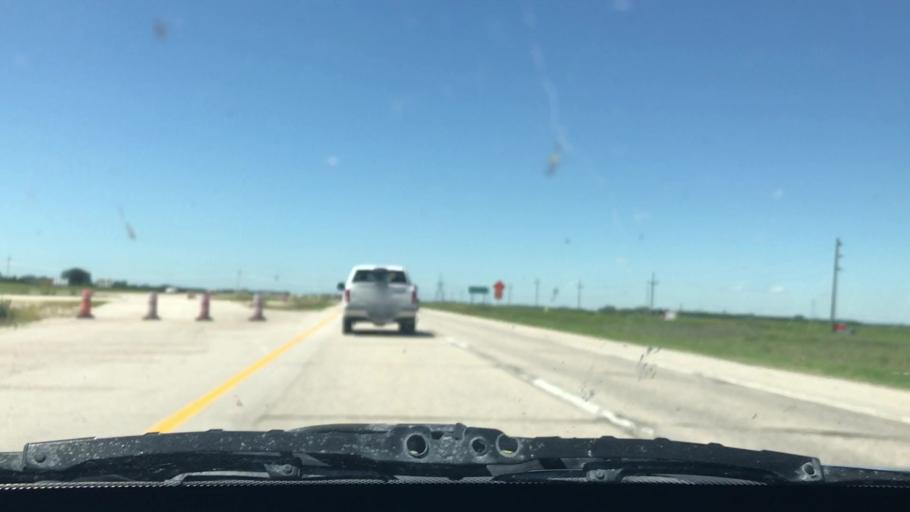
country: CA
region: Manitoba
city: Steinbach
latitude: 49.7066
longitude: -96.6593
